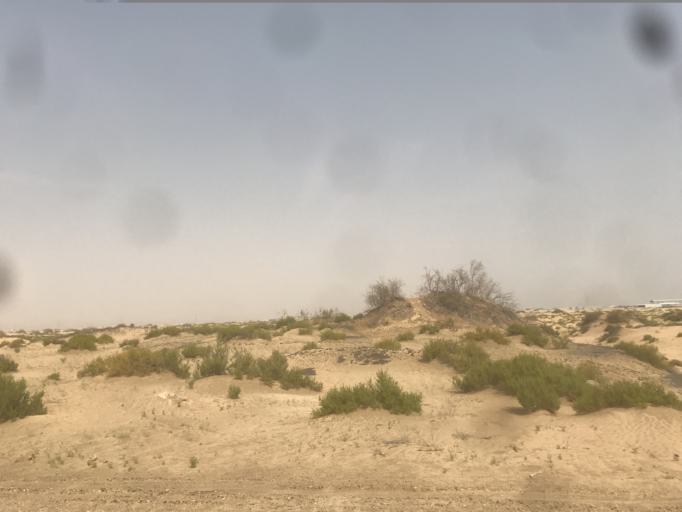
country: SA
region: Eastern Province
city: Abqaiq
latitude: 25.9096
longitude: 49.9380
